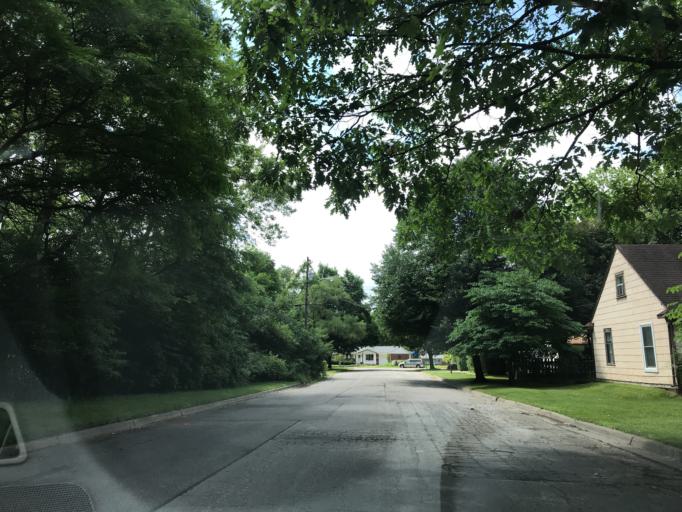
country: US
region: Michigan
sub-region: Washtenaw County
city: Ann Arbor
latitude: 42.2398
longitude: -83.7025
